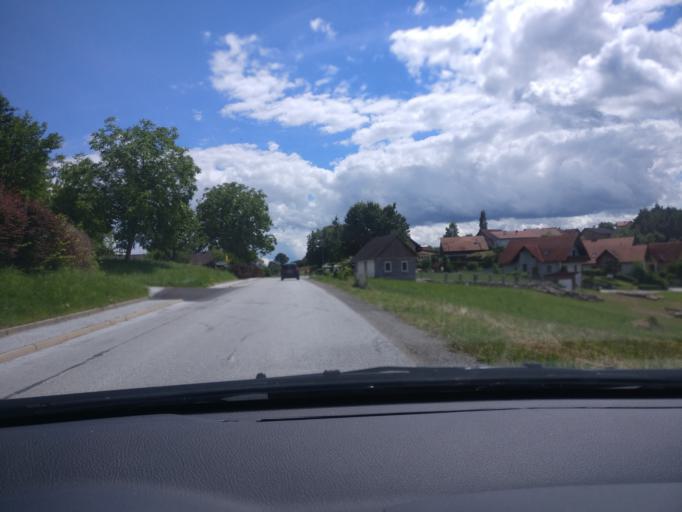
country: AT
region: Styria
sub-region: Politischer Bezirk Weiz
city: Nitscha
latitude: 47.1249
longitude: 15.7335
